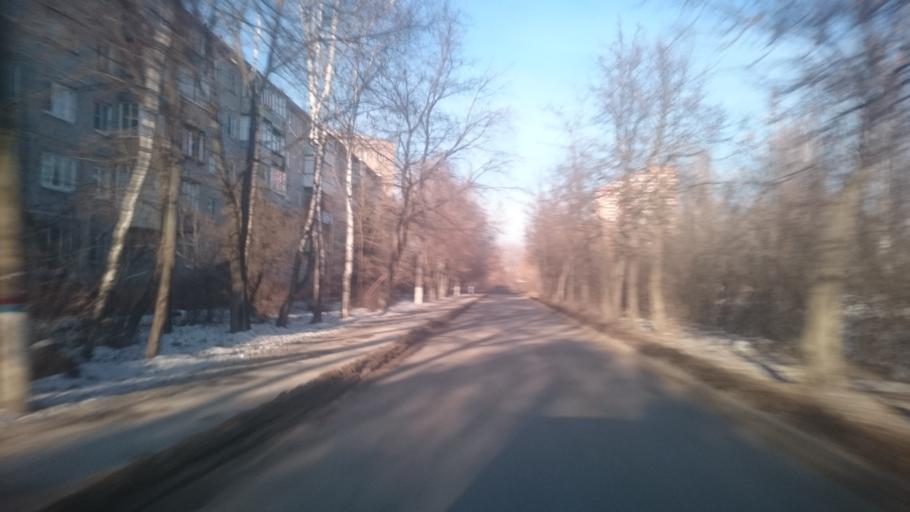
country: RU
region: Tula
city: Tula
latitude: 54.1786
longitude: 37.6419
